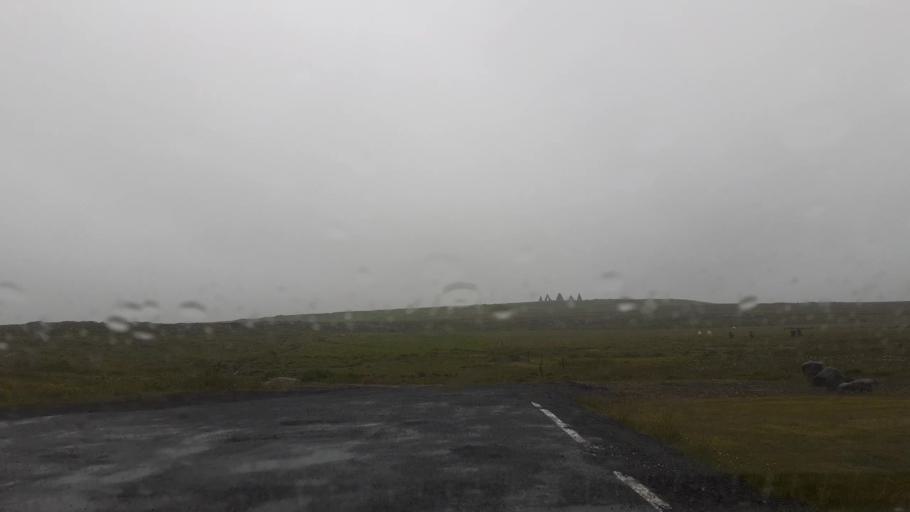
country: IS
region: Northeast
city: Husavik
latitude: 66.4559
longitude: -15.9545
